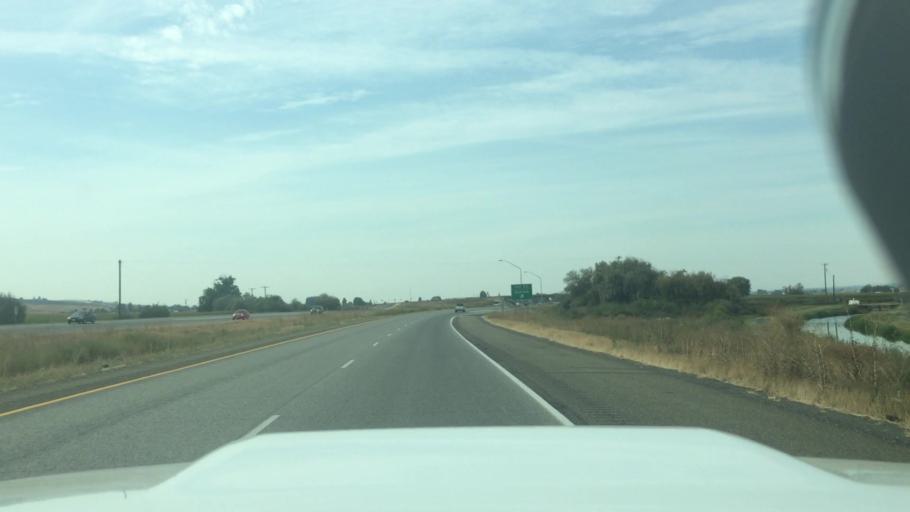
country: US
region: Washington
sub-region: Yakima County
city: Sunnyside
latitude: 46.3234
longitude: -120.0705
